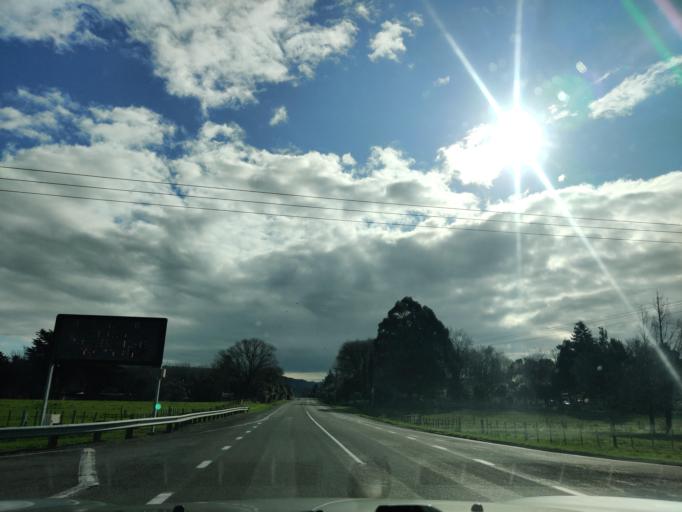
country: NZ
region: Manawatu-Wanganui
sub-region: Palmerston North City
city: Palmerston North
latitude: -40.3406
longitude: 175.8800
